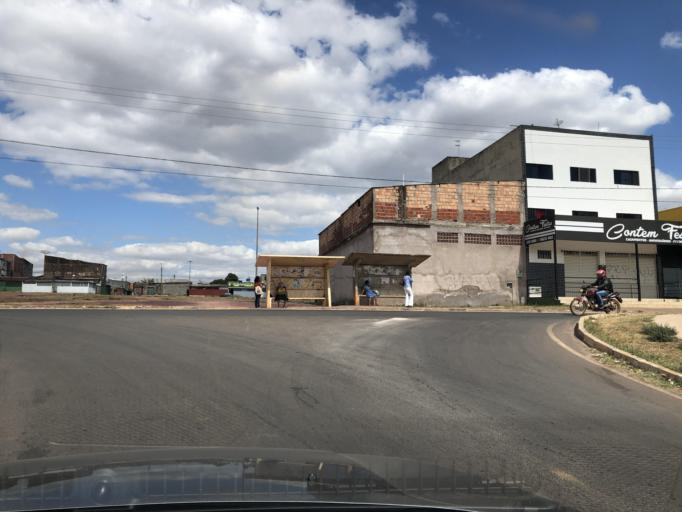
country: BR
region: Federal District
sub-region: Brasilia
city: Brasilia
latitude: -15.8896
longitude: -48.1430
